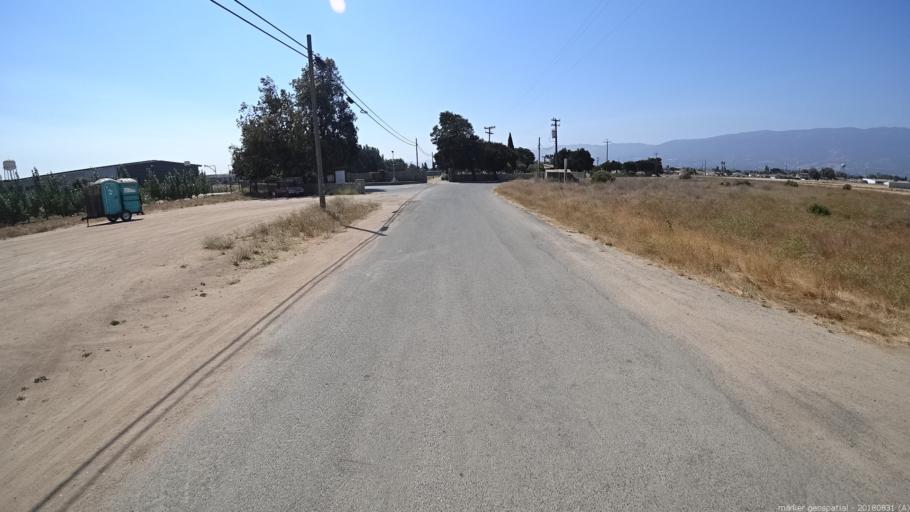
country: US
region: California
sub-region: Monterey County
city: Soledad
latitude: 36.4296
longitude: -121.3120
